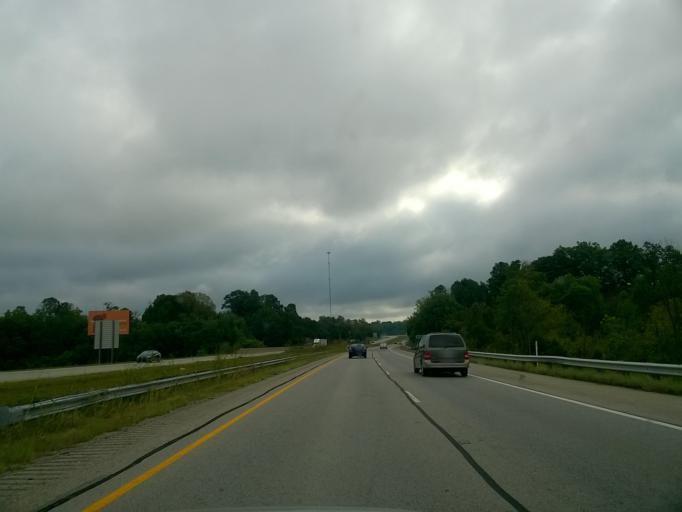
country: US
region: Indiana
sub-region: Harrison County
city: Corydon
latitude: 38.2434
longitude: -86.1018
